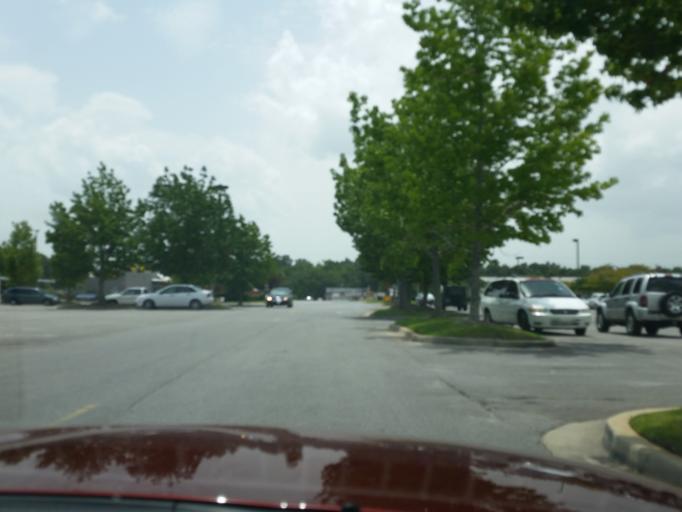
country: US
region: Florida
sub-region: Escambia County
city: Ensley
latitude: 30.5289
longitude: -87.2735
